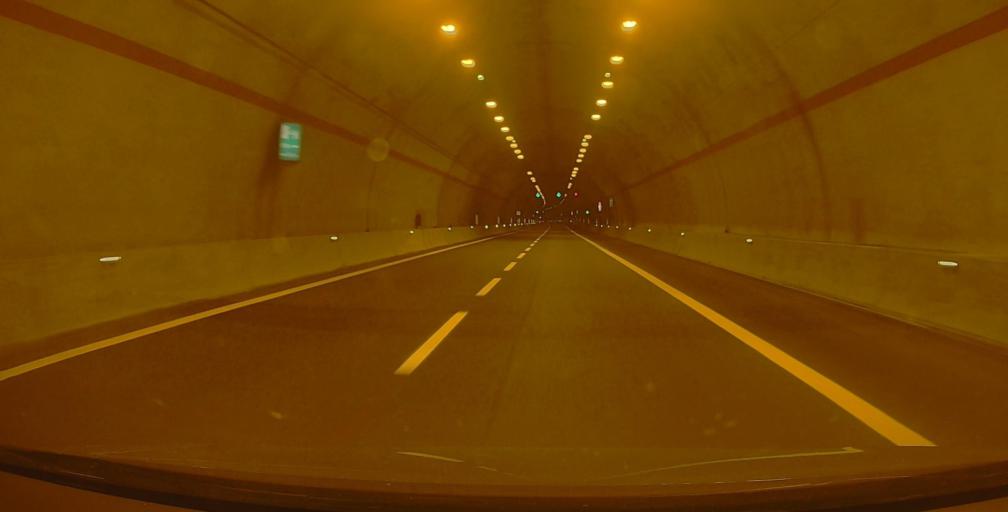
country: IT
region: Calabria
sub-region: Provincia di Catanzaro
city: Martirano
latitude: 39.1009
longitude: 16.2414
